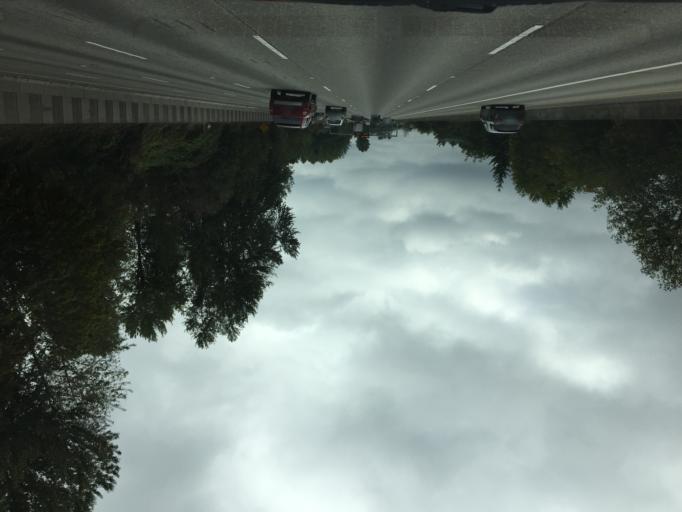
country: US
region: Washington
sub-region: King County
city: Tukwila
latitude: 47.4510
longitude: -122.2657
